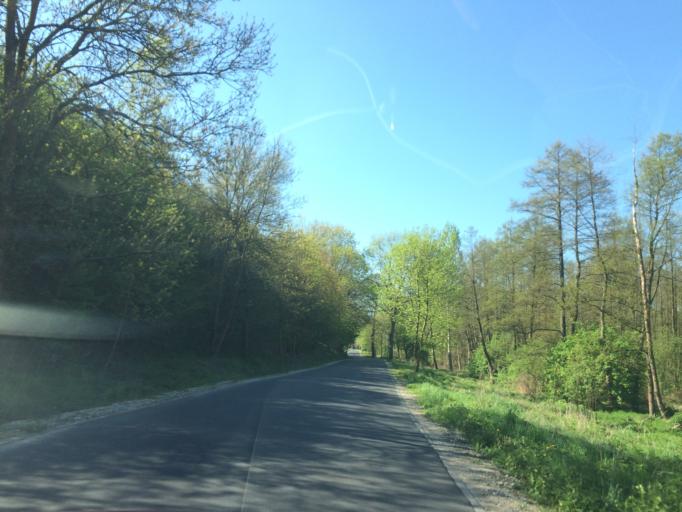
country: PL
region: Warmian-Masurian Voivodeship
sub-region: Powiat nowomiejski
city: Nowe Miasto Lubawskie
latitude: 53.4878
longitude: 19.5757
